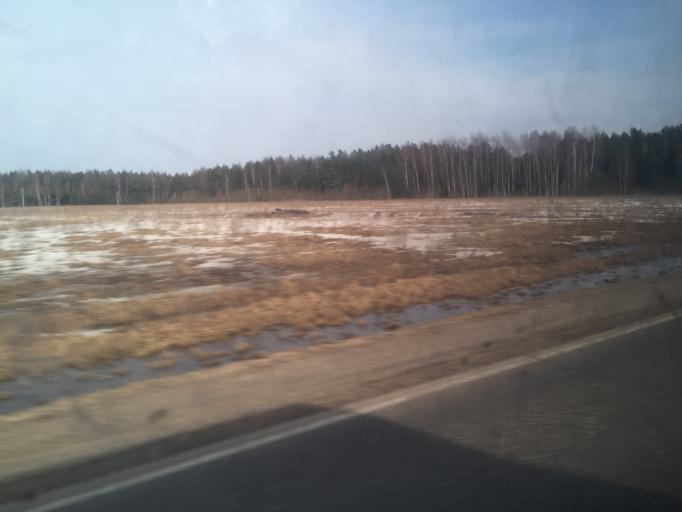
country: RU
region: Ivanovo
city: Lezhnevo
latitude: 56.8292
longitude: 40.8896
